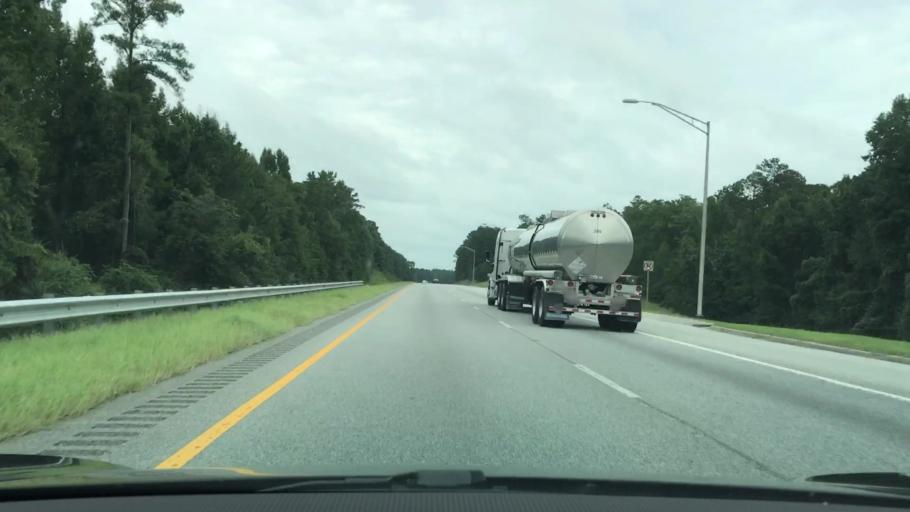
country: US
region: Alabama
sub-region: Macon County
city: Tuskegee
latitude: 32.5008
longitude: -85.6126
